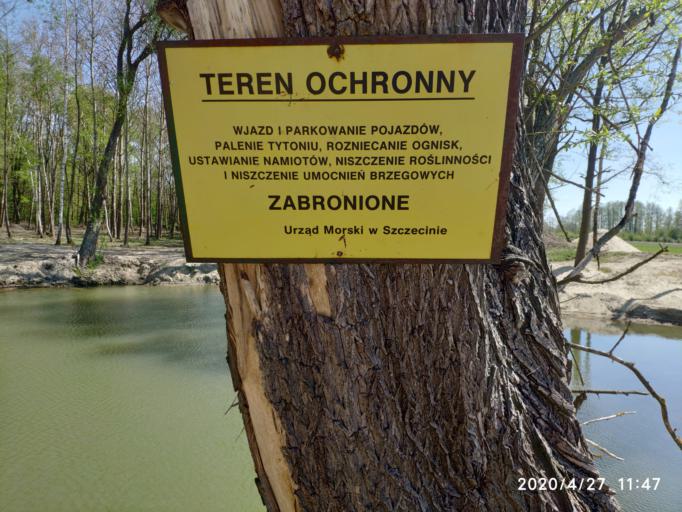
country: PL
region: Lubusz
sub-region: Powiat zielonogorski
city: Sulechow
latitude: 52.0231
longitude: 15.6160
